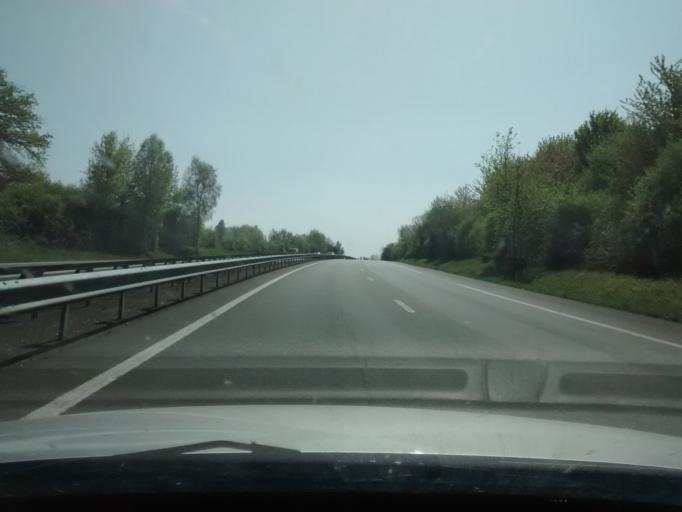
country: FR
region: Pays de la Loire
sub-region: Departement de la Sarthe
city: Coulaines
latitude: 48.0323
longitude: 0.2134
